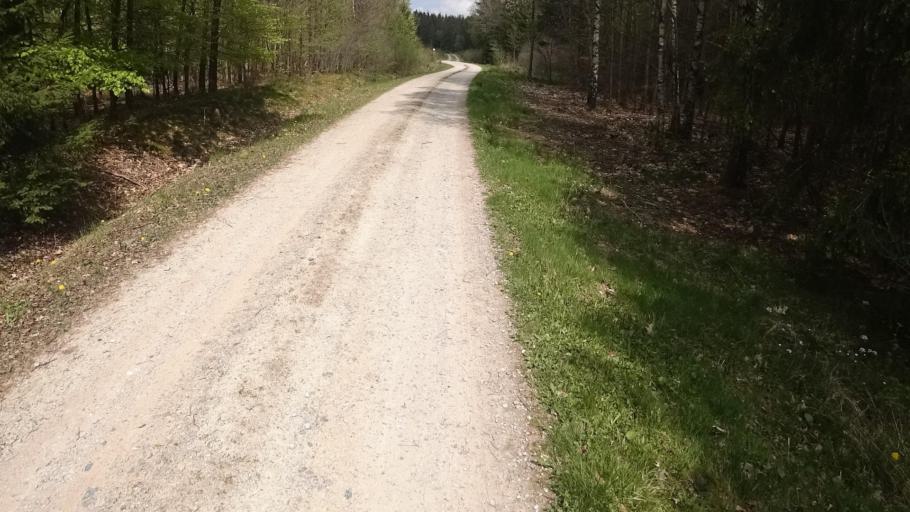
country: DE
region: Rheinland-Pfalz
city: Maisborn
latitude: 50.0693
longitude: 7.5845
